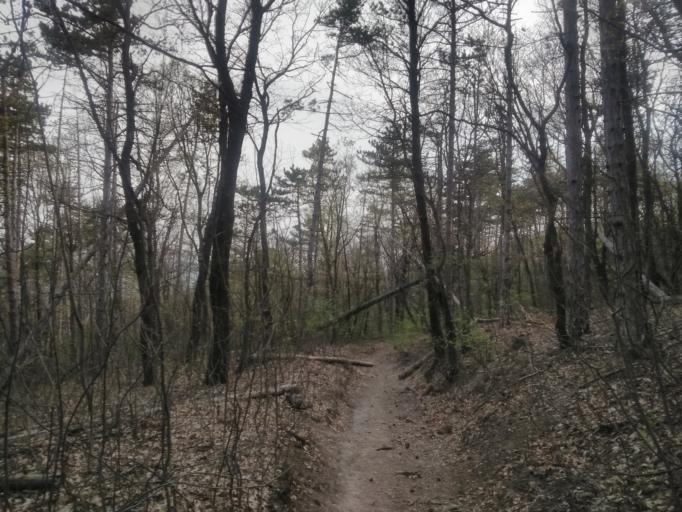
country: HU
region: Pest
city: Leanyfalu
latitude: 47.7442
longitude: 19.0619
